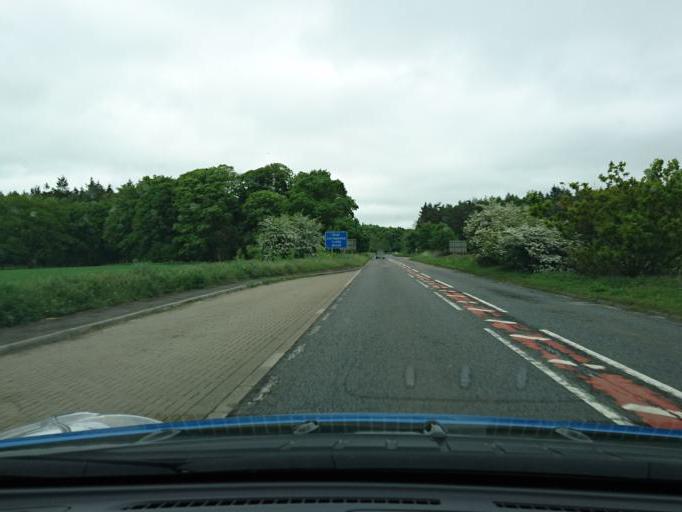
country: GB
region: England
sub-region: Oxfordshire
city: Frilford
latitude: 51.6927
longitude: -1.3666
